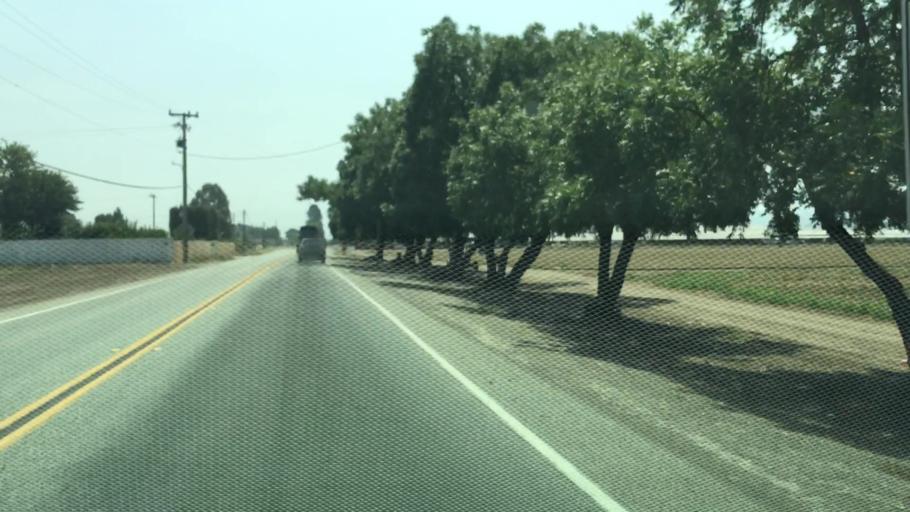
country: US
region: California
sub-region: Santa Clara County
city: Gilroy
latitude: 37.0332
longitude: -121.5322
